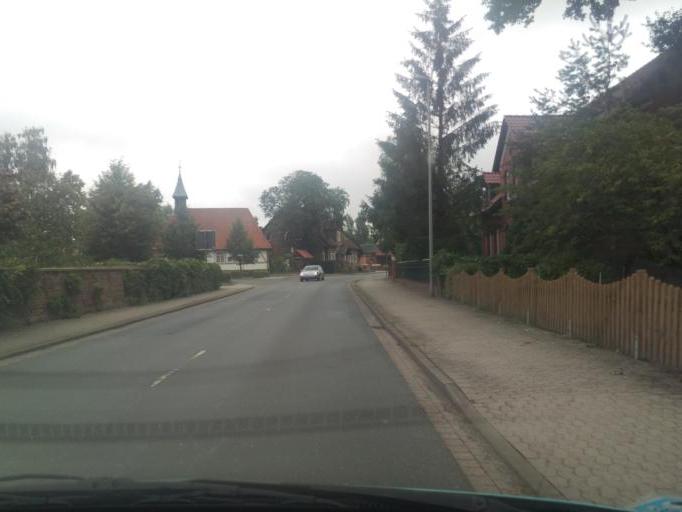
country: DE
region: Lower Saxony
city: Dollbergen
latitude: 52.3860
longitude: 10.1730
